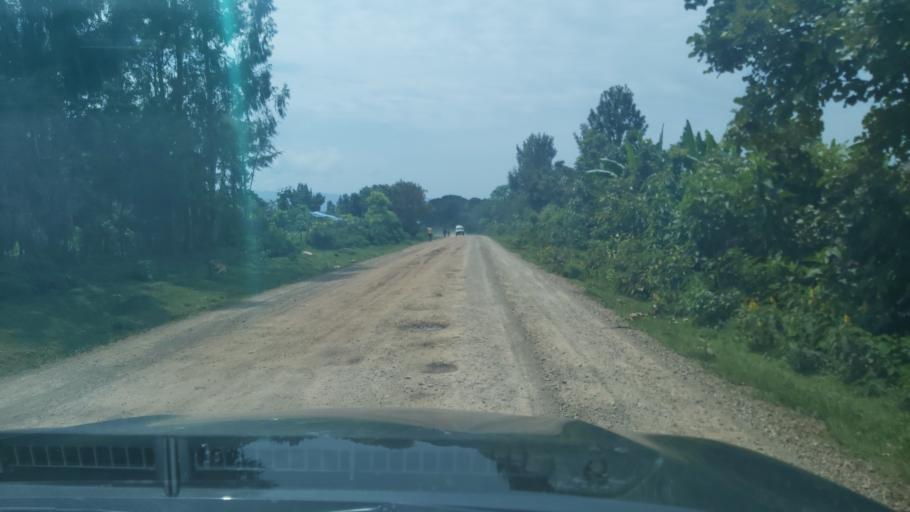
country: ET
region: Oromiya
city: Jima
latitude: 7.7401
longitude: 36.7790
